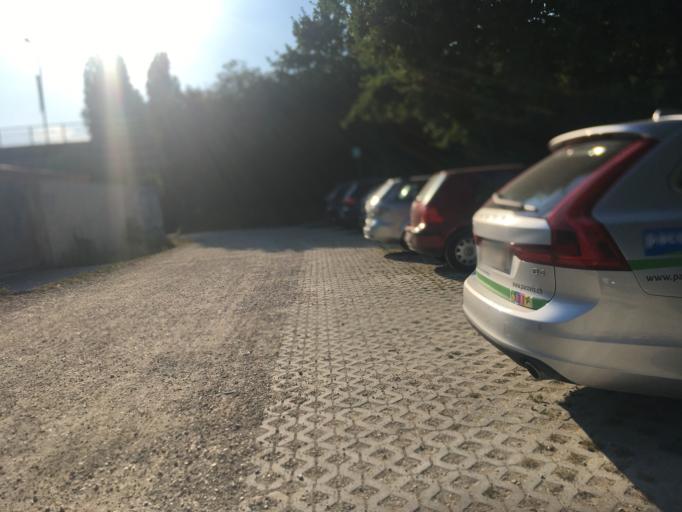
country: CH
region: Bern
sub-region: Biel/Bienne District
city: Bellmund
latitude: 47.1194
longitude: 7.2582
